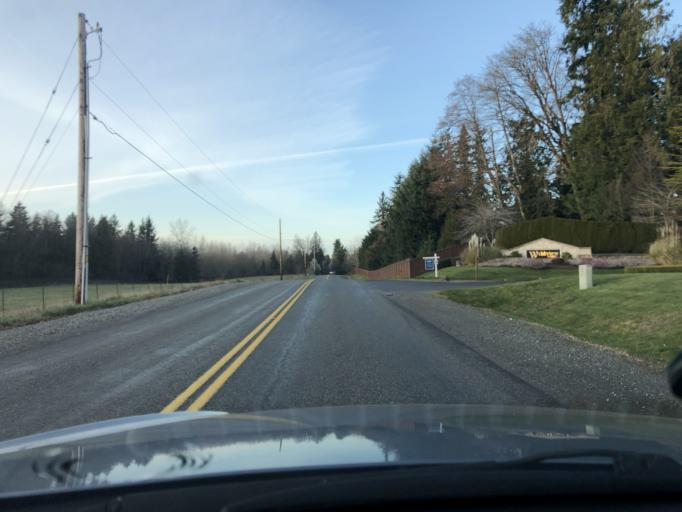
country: US
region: Washington
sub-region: Pierce County
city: Bonney Lake
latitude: 47.2037
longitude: -122.1227
